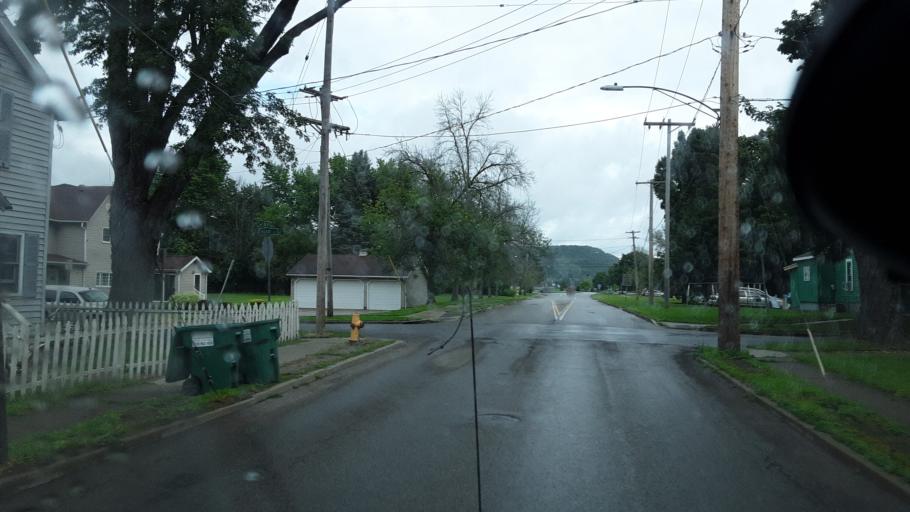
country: US
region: New York
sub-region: Cattaraugus County
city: Olean
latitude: 42.0829
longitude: -78.4447
